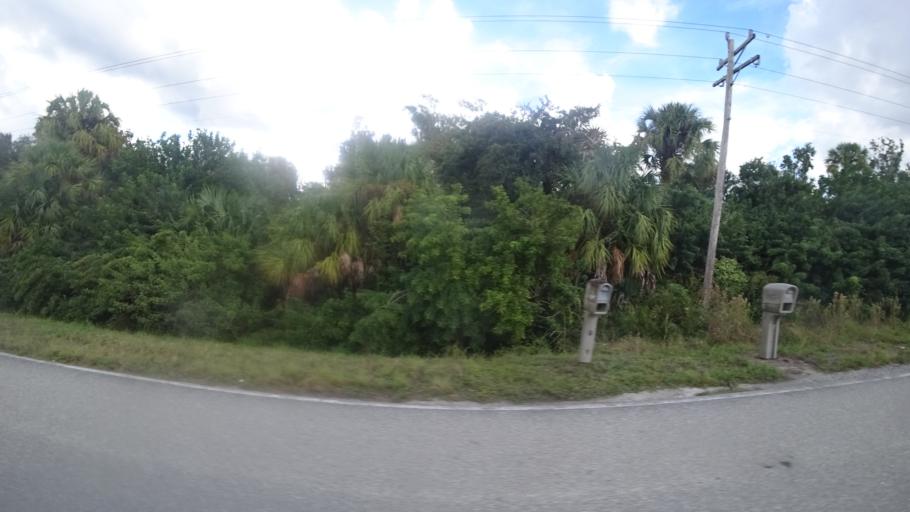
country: US
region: Florida
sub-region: Manatee County
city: Memphis
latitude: 27.6107
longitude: -82.5273
